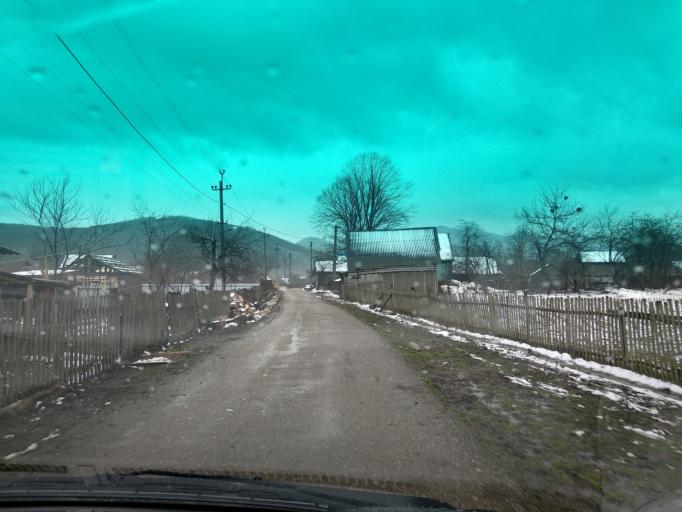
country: RU
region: Krasnodarskiy
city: Khadyzhensk
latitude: 44.2112
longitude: 39.4217
